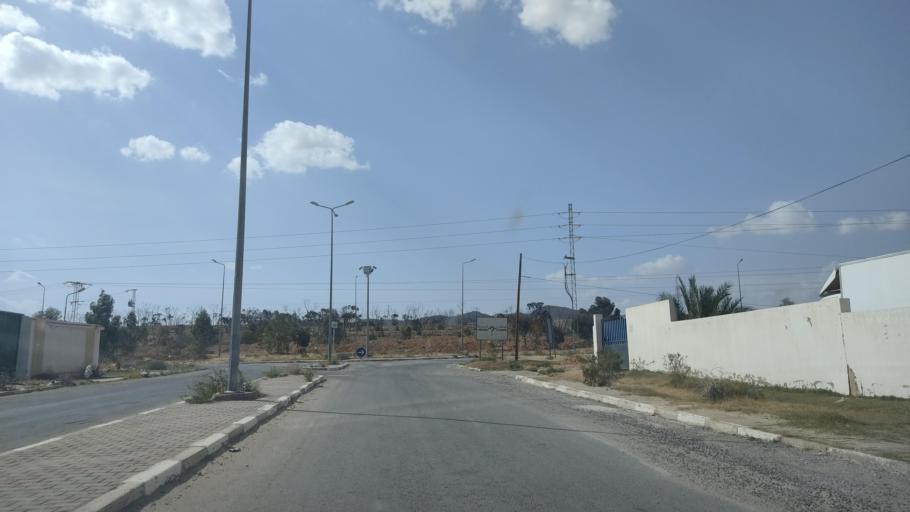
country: TN
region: Sidi Bu Zayd
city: Sidi Bouzid
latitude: 35.1089
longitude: 9.5427
